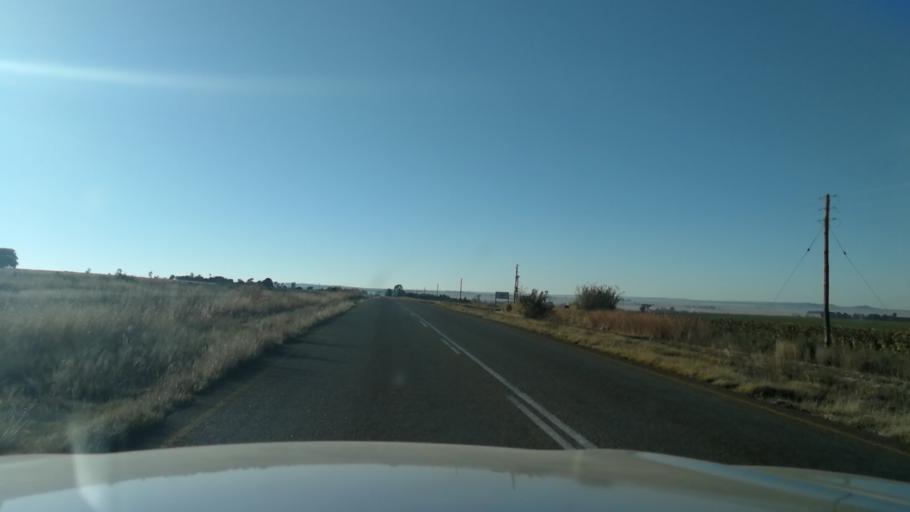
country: ZA
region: North-West
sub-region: Bojanala Platinum District Municipality
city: Koster
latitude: -25.9168
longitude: 27.0731
